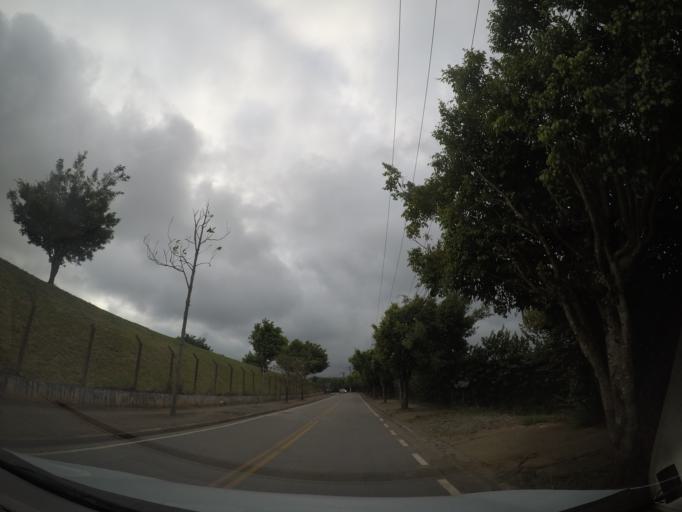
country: BR
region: Sao Paulo
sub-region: Aruja
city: Aruja
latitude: -23.4031
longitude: -46.3532
